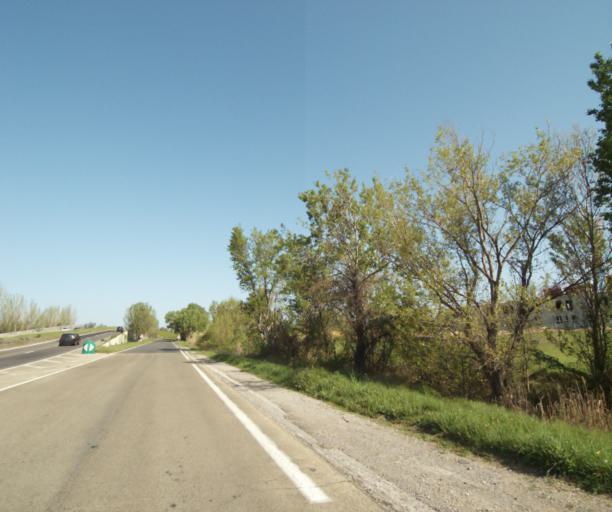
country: FR
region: Languedoc-Roussillon
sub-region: Departement de l'Herault
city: Perols
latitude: 43.5781
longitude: 3.9472
